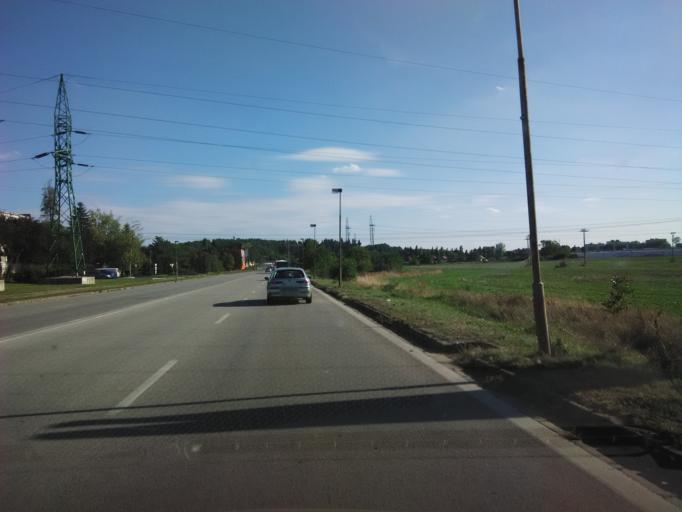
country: SK
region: Nitriansky
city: Levice
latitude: 48.2332
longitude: 18.5999
